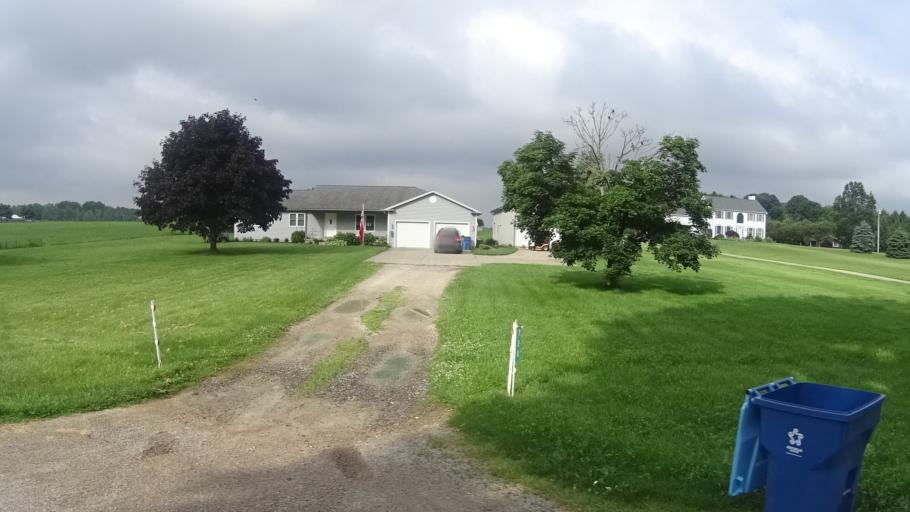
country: US
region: Ohio
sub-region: Erie County
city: Huron
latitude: 41.3793
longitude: -82.5326
